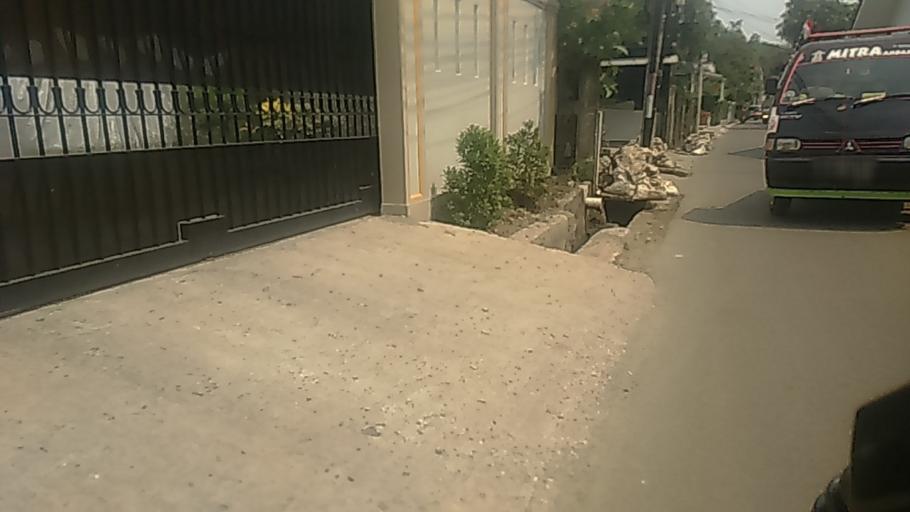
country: ID
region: West Java
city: Pamulang
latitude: -6.3259
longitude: 106.8061
